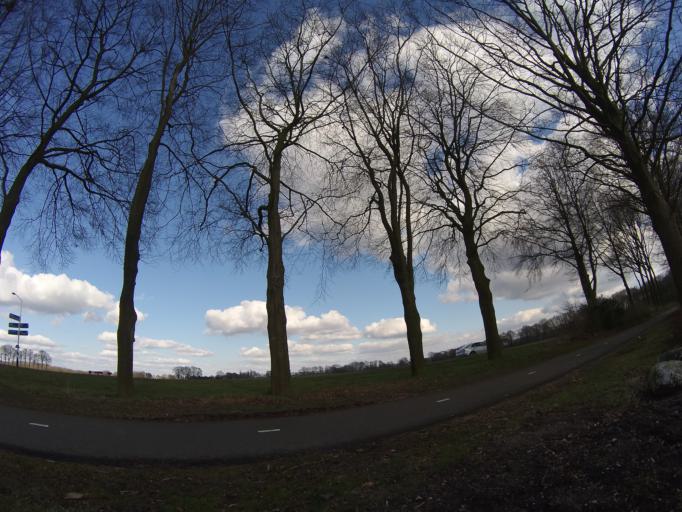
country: NL
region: Drenthe
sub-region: Gemeente Coevorden
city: Sleen
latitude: 52.7699
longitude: 6.8065
